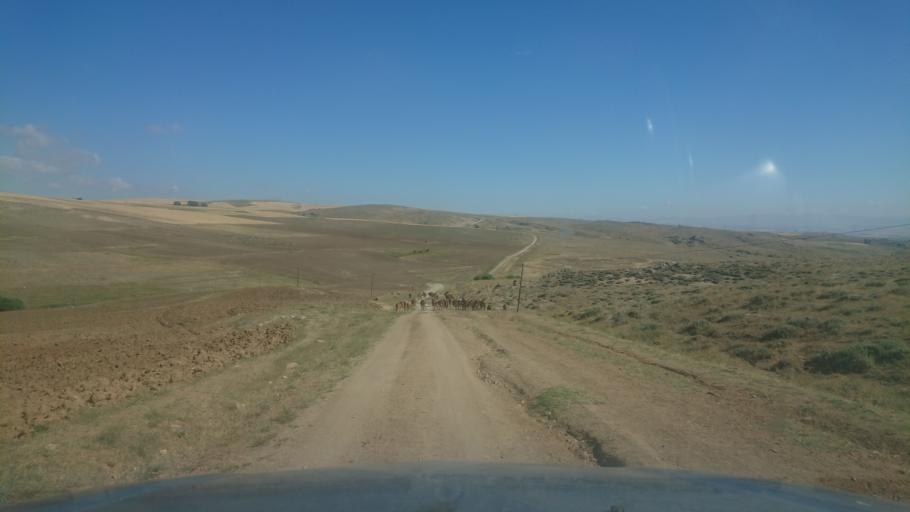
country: TR
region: Aksaray
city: Agacoren
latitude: 38.9102
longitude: 33.8564
